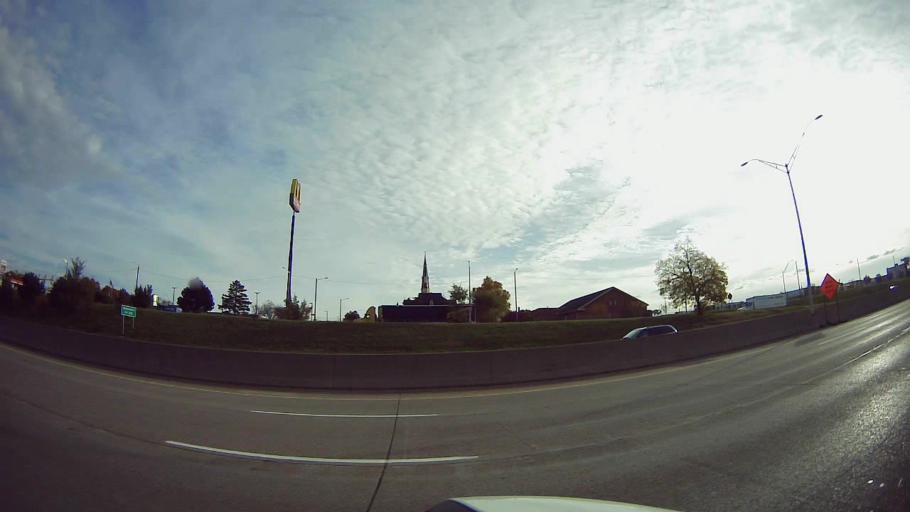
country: US
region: Michigan
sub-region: Wayne County
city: Detroit
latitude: 42.3504
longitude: -83.0477
